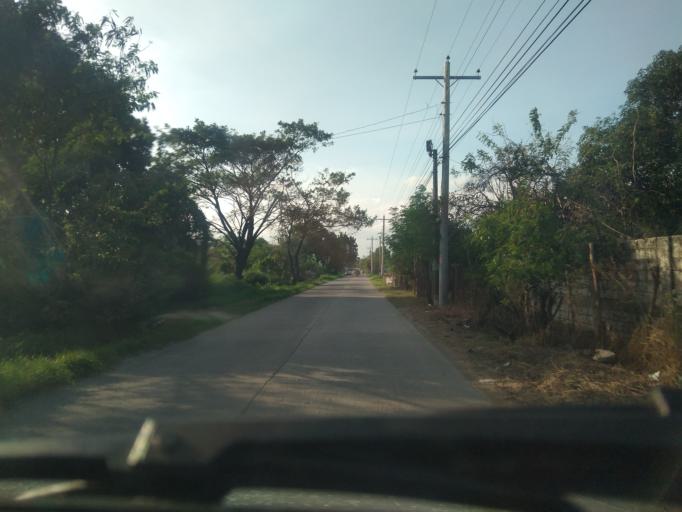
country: PH
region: Central Luzon
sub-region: Province of Pampanga
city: Mexico
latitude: 15.0854
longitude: 120.6965
